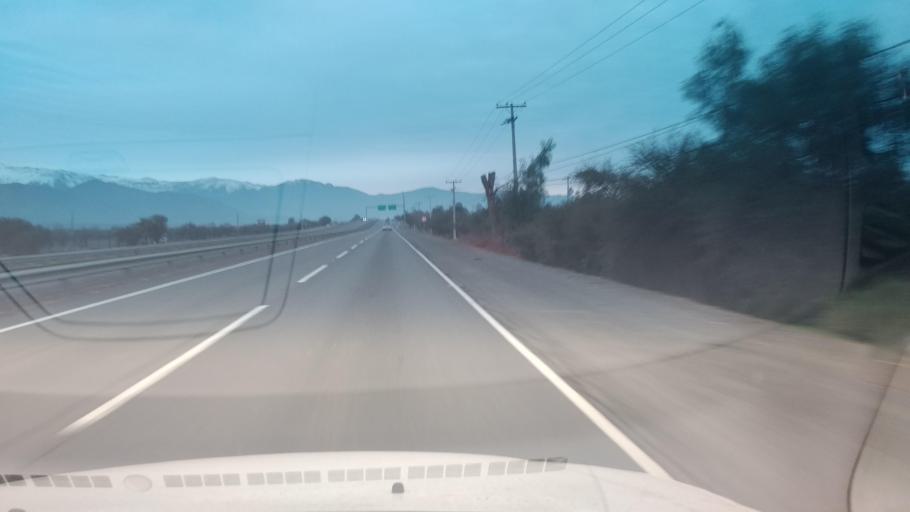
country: CL
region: Santiago Metropolitan
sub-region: Provincia de Chacabuco
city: Chicureo Abajo
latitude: -33.1416
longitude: -70.6619
